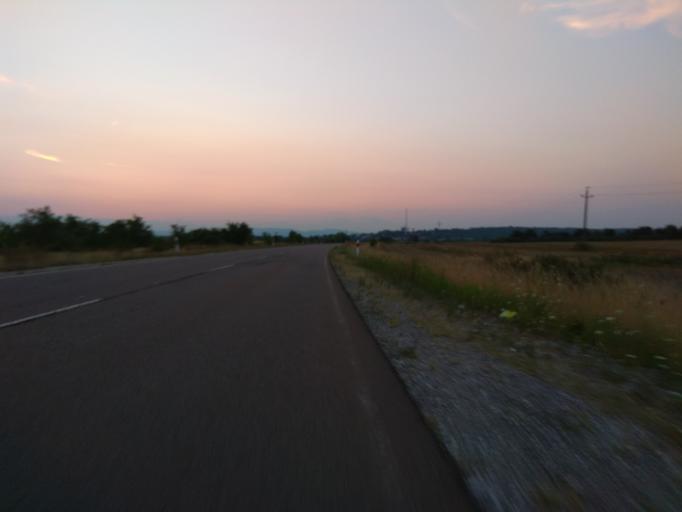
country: HU
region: Borsod-Abauj-Zemplen
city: Emod
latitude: 47.9267
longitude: 20.8347
